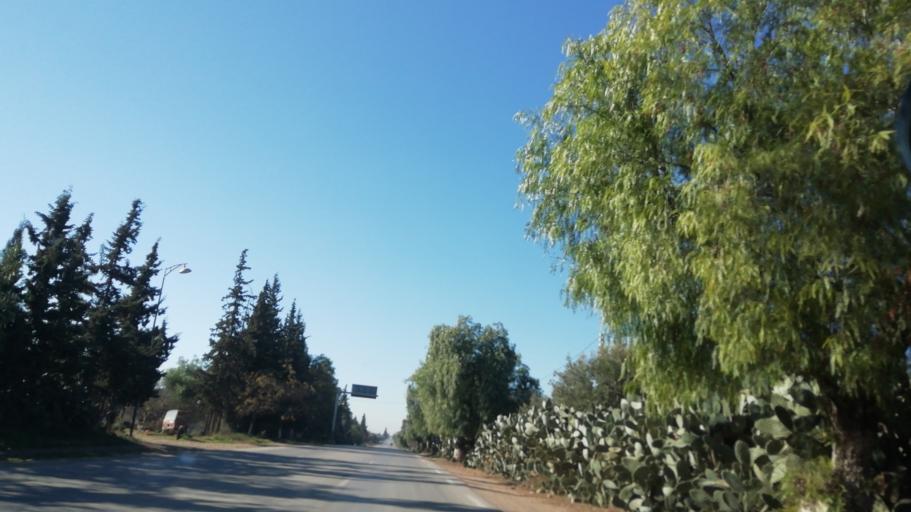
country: DZ
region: Tlemcen
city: Nedroma
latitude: 34.8366
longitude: -1.7816
